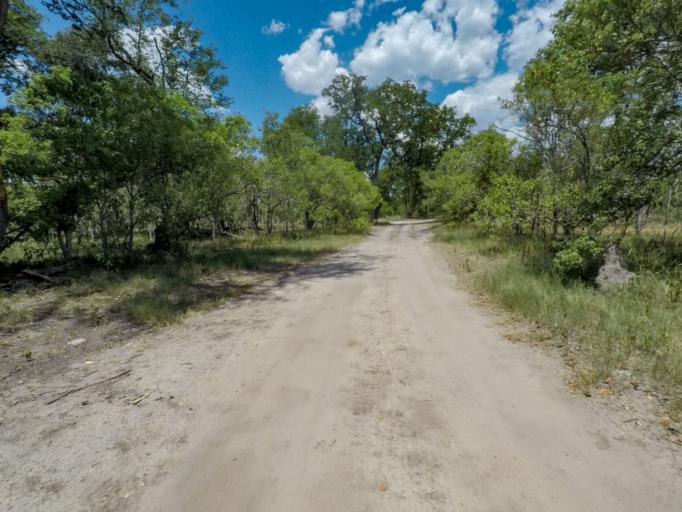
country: BW
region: North West
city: Maun
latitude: -19.1737
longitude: 23.7514
